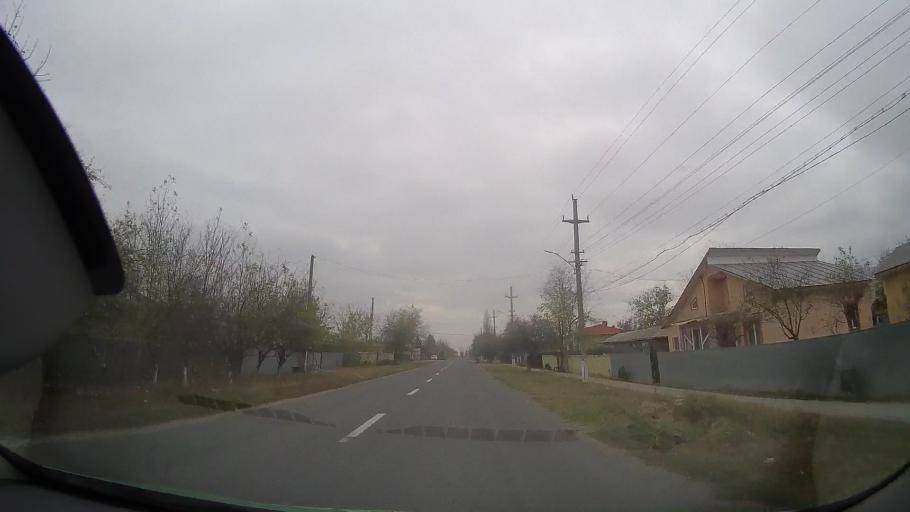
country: RO
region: Ialomita
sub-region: Comuna Garbovi
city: Garbovi
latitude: 44.7847
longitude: 26.7596
